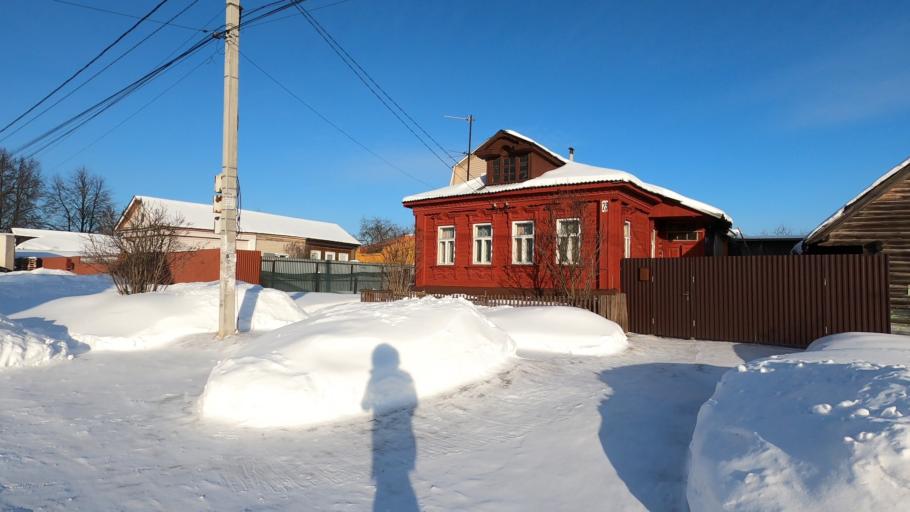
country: RU
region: Moskovskaya
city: Pavlovskiy Posad
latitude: 55.7685
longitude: 38.6984
